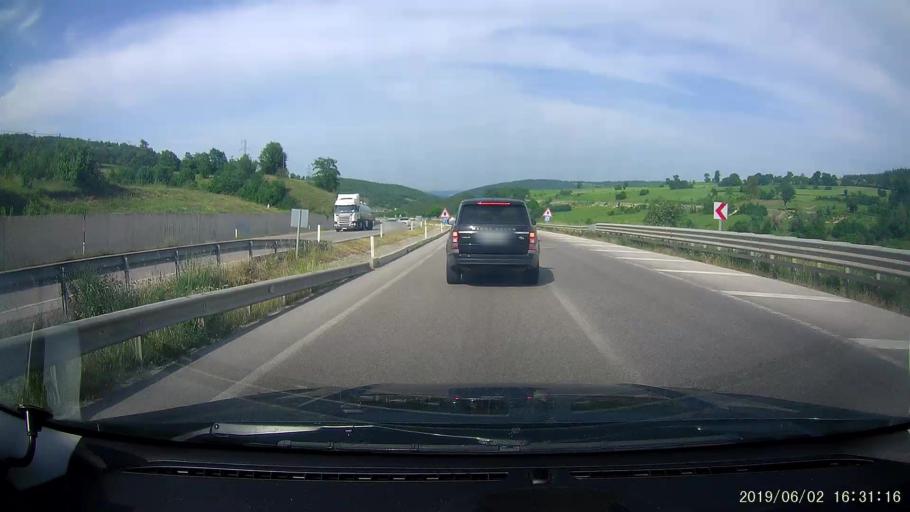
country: TR
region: Samsun
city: Ladik
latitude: 41.0306
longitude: 35.8985
